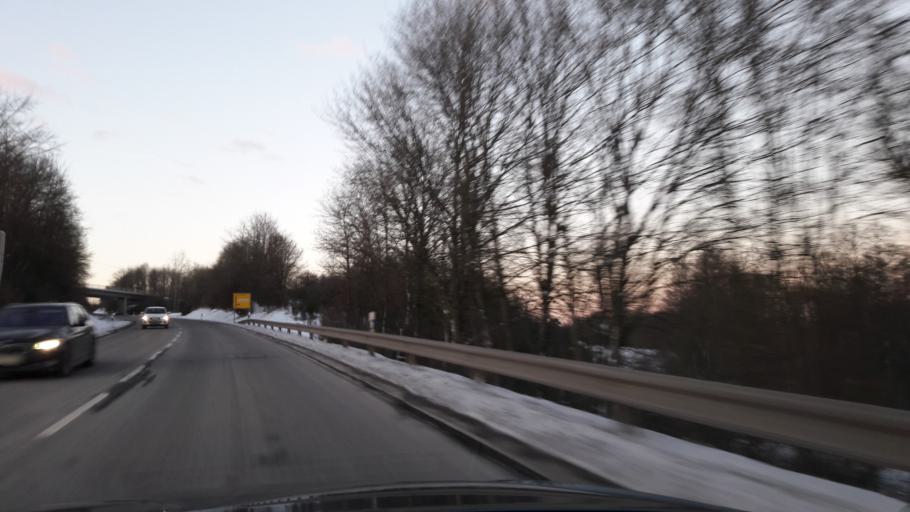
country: DE
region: Rheinland-Pfalz
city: Reichenbach
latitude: 49.6416
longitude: 7.2947
